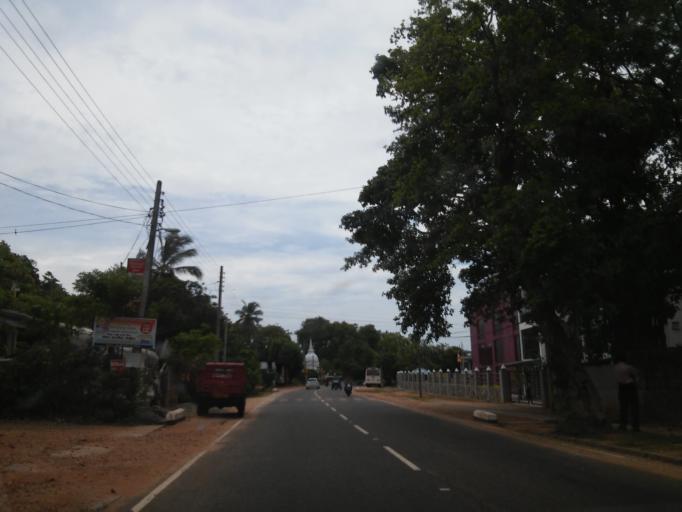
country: LK
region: Eastern Province
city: Trincomalee
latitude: 8.5904
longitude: 81.2157
